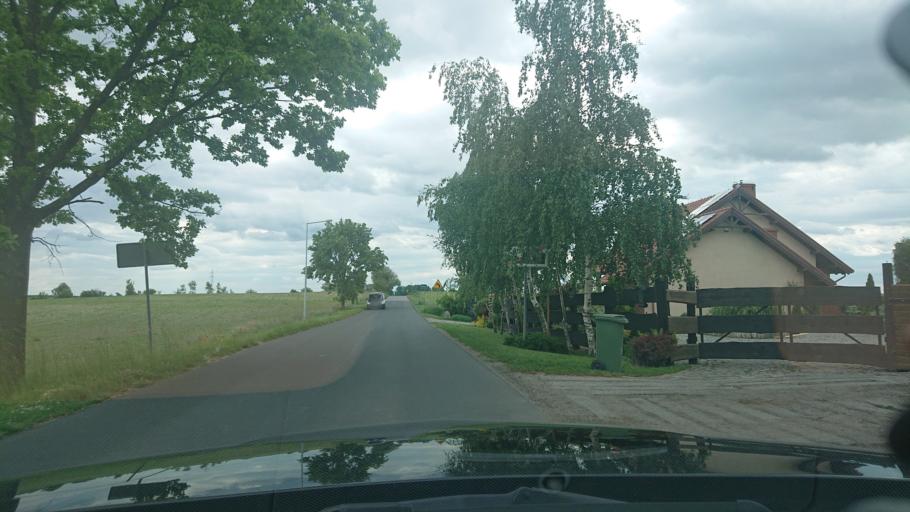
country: PL
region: Greater Poland Voivodeship
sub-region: Powiat gnieznienski
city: Gniezno
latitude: 52.5403
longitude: 17.5366
